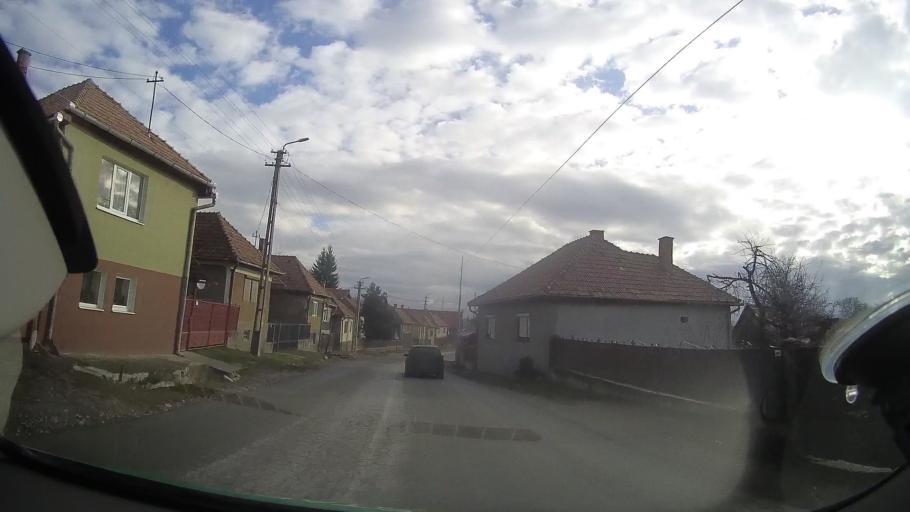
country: RO
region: Cluj
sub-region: Comuna Baisoara
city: Baisoara
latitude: 46.6184
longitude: 23.4558
